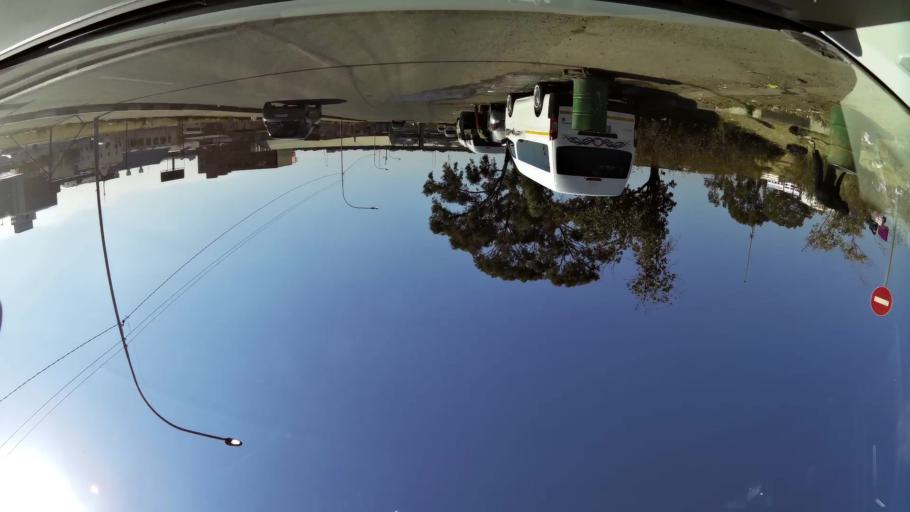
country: ZA
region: Gauteng
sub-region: City of Johannesburg Metropolitan Municipality
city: Johannesburg
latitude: -26.2088
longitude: 28.0330
